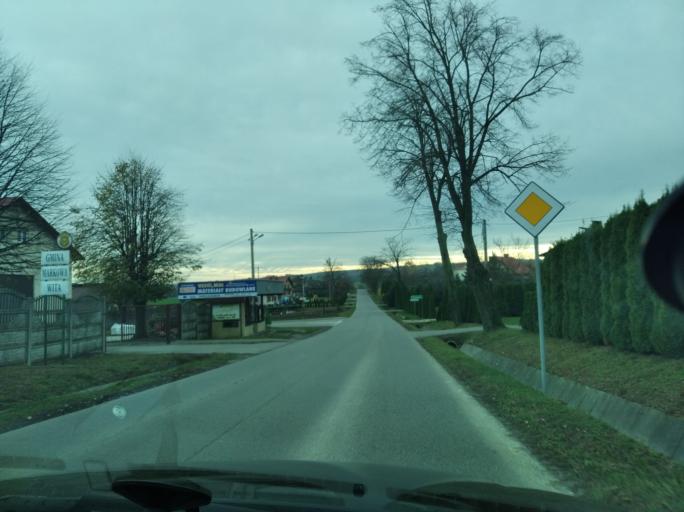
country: PL
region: Subcarpathian Voivodeship
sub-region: Powiat lancucki
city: Wysoka
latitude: 50.0198
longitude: 22.2609
